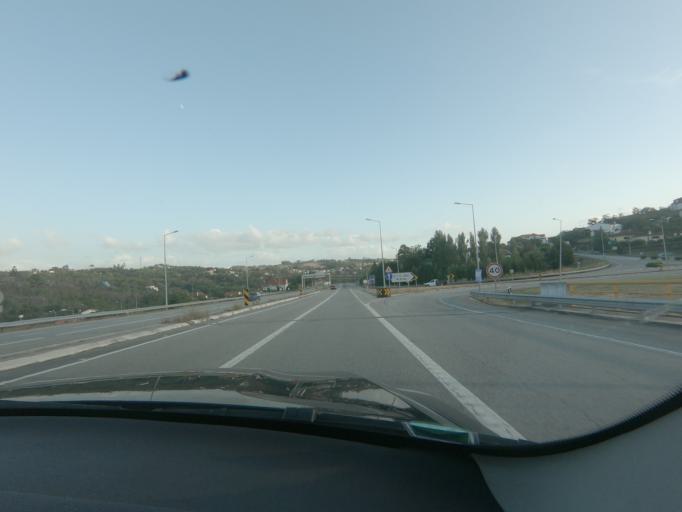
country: PT
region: Viseu
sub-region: Santa Comba Dao
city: Santa Comba Dao
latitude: 40.4002
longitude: -8.1263
